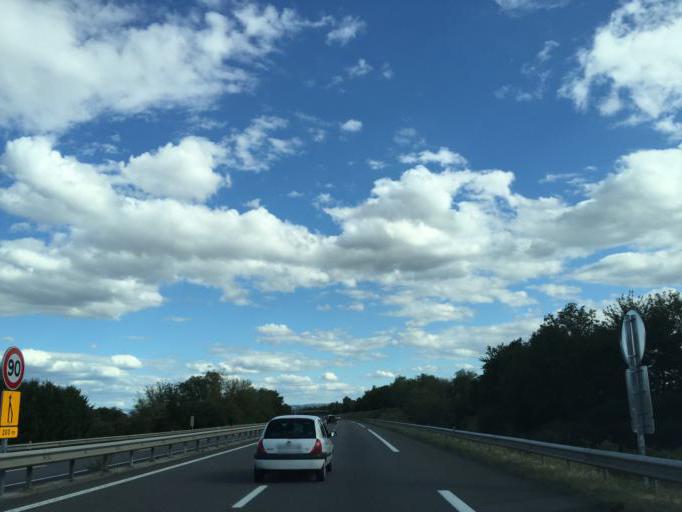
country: FR
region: Rhone-Alpes
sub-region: Departement de la Loire
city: Saint-Cyprien
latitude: 45.5774
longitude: 4.2167
